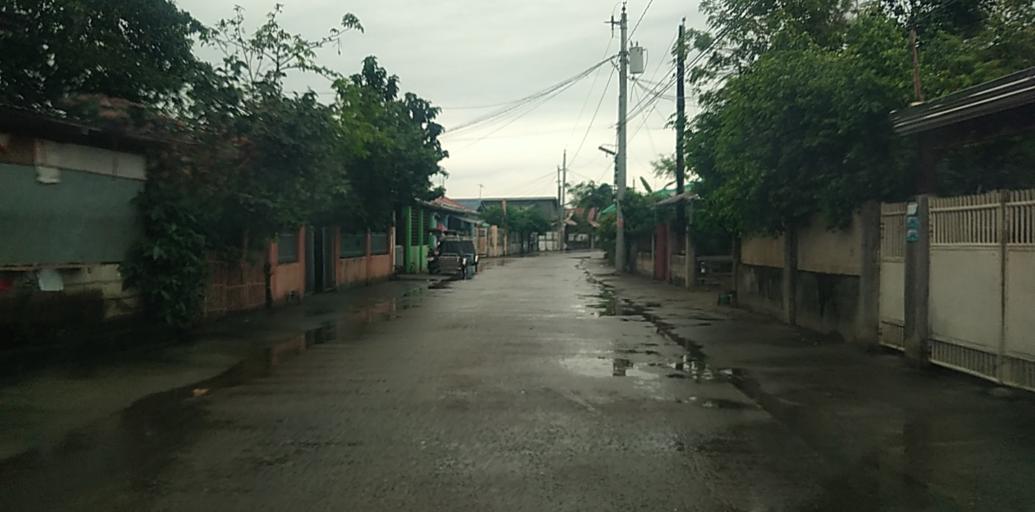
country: PH
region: Central Luzon
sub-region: Province of Pampanga
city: Arayat
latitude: 15.1410
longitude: 120.7337
